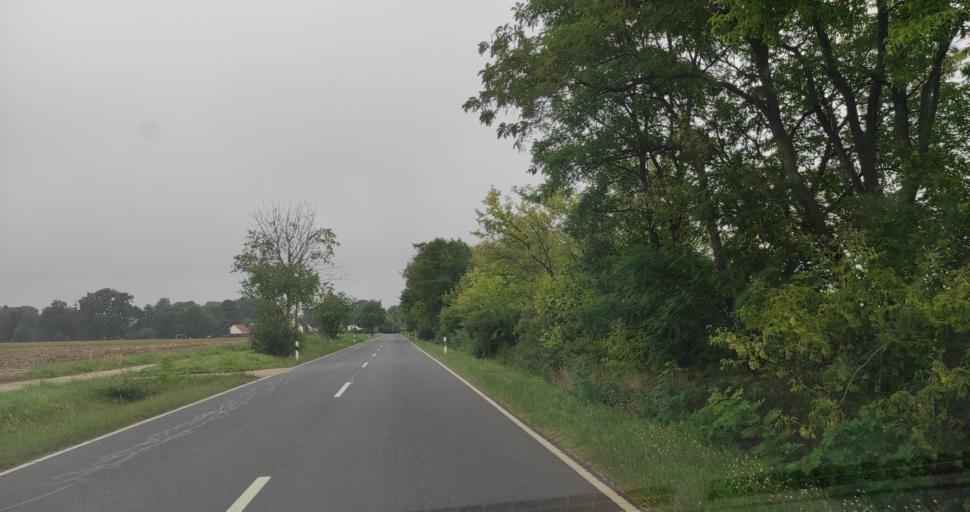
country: DE
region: Brandenburg
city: Forst
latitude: 51.6895
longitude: 14.6171
